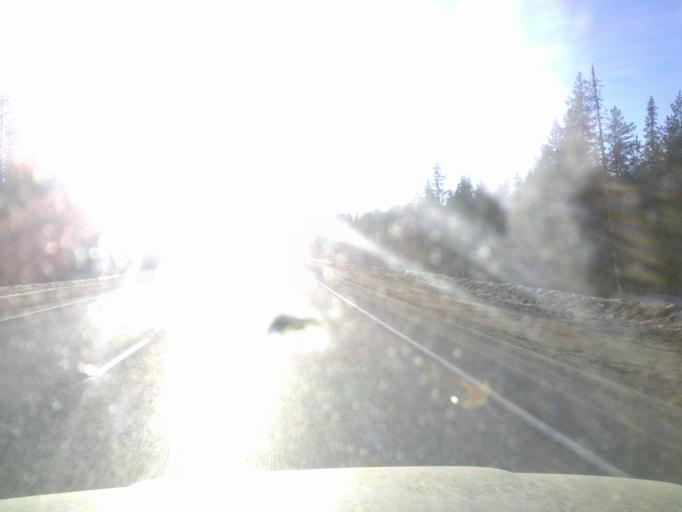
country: RU
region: Republic of Karelia
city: Medvezh'yegorsk
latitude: 62.8372
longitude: 34.3134
